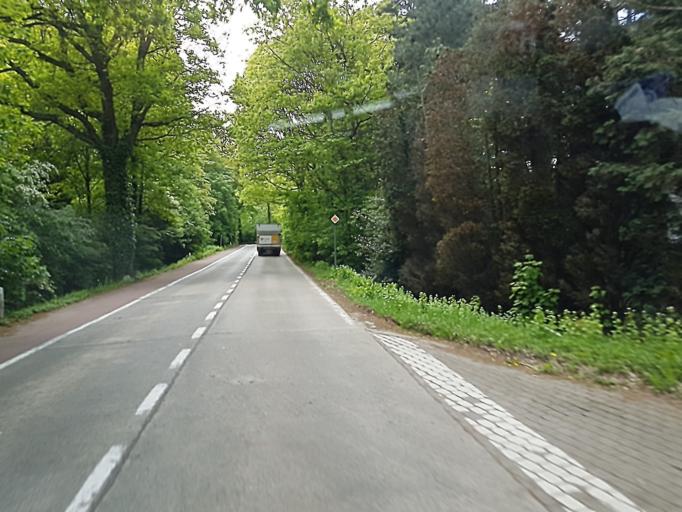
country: BE
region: Flanders
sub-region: Provincie Vlaams-Brabant
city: Diest
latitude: 50.9959
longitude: 5.0325
